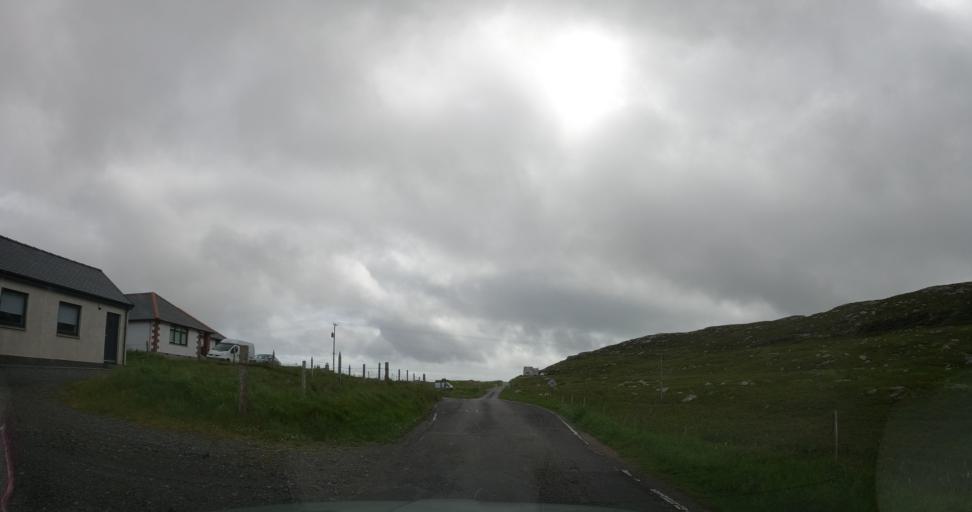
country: GB
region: Scotland
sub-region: Eilean Siar
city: Barra
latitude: 56.9649
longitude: -7.5113
